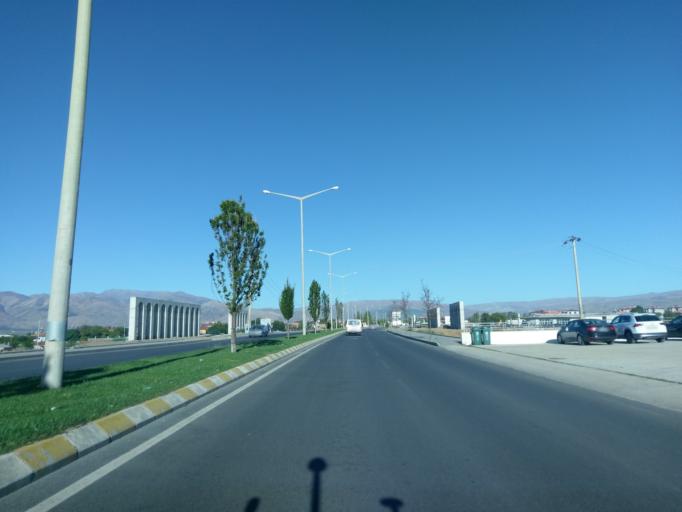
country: TR
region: Erzincan
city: Erzincan
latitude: 39.7494
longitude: 39.4617
